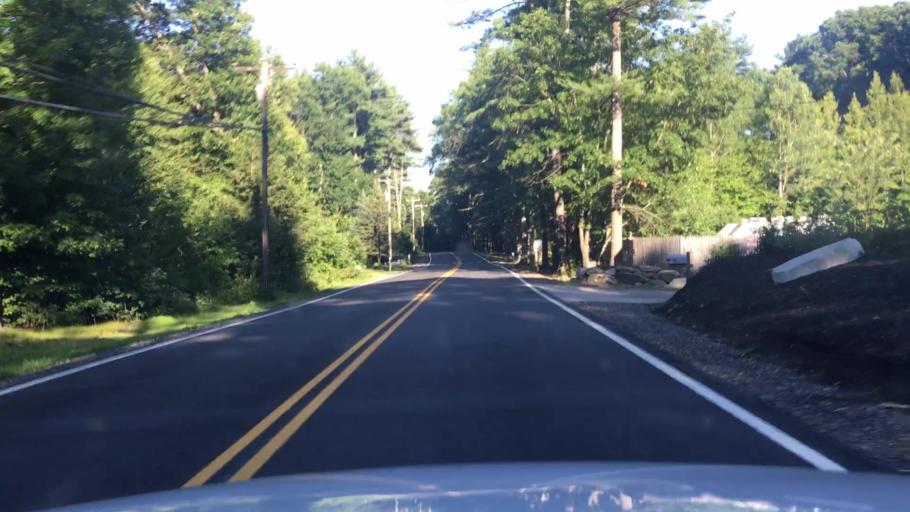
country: US
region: New Hampshire
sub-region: Rockingham County
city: Sandown
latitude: 42.9129
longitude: -71.1797
